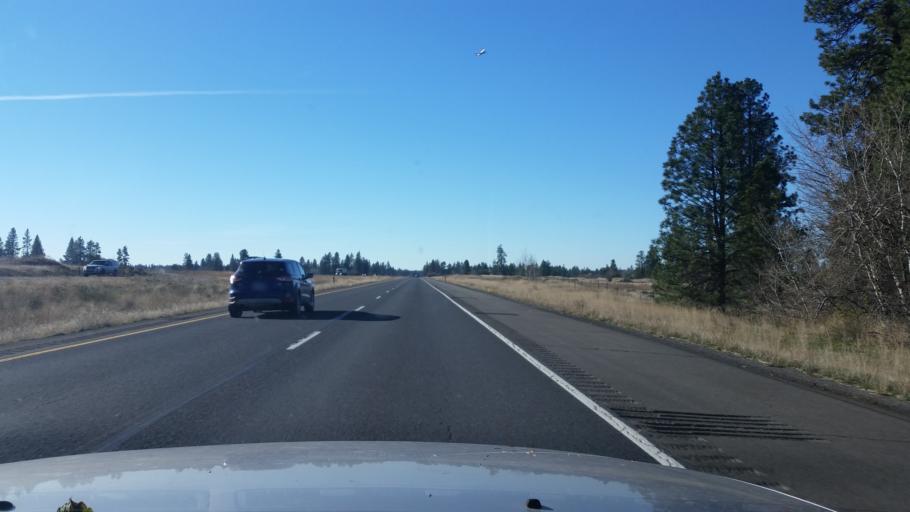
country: US
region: Washington
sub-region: Spokane County
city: Medical Lake
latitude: 47.5440
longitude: -117.6329
